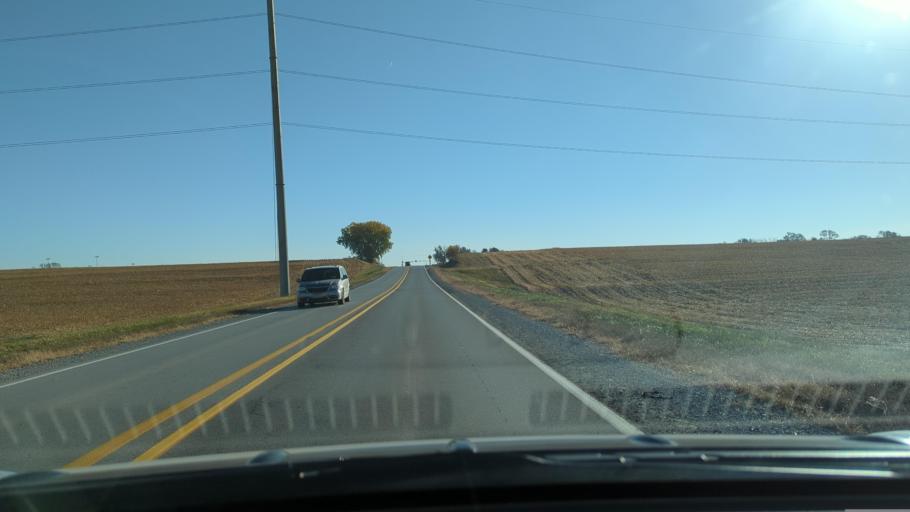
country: US
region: Nebraska
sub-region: Sarpy County
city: Springfield
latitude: 41.0889
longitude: -96.0897
